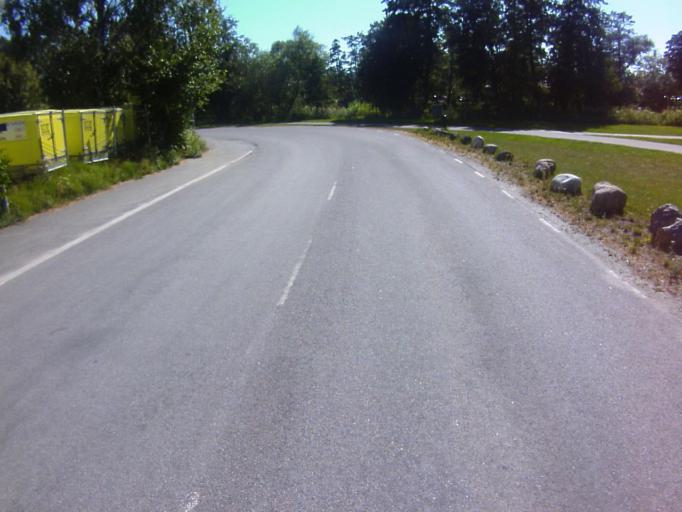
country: SE
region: Soedermanland
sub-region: Eskilstuna Kommun
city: Eskilstuna
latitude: 59.3816
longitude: 16.5005
